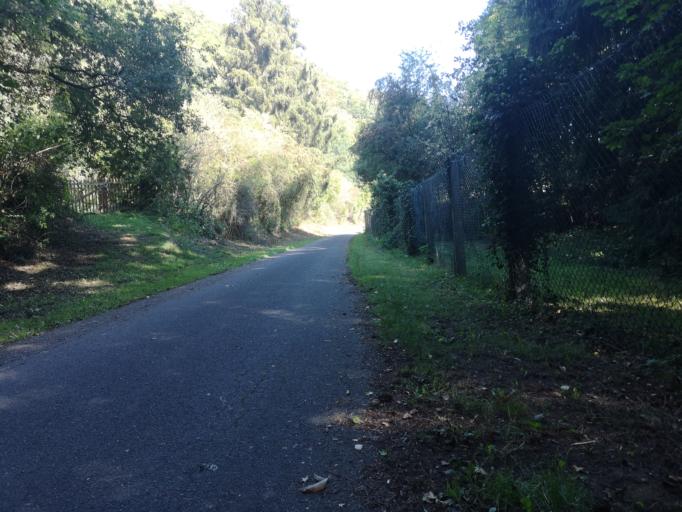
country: DE
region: North Rhine-Westphalia
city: Heimbach
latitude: 50.6412
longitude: 6.4668
